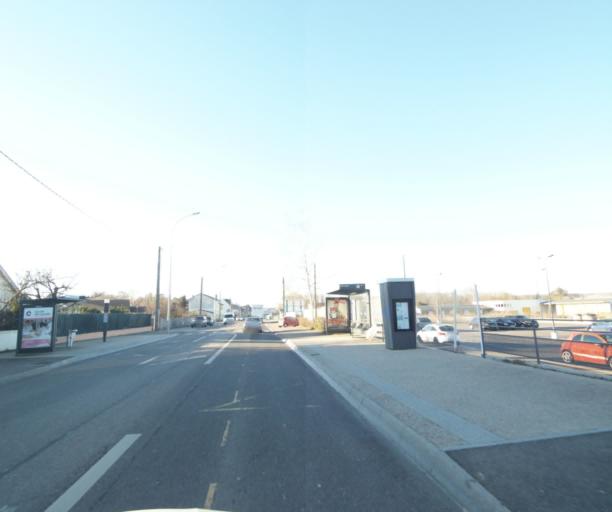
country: FR
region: Lorraine
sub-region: Departement de Meurthe-et-Moselle
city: Laneuveville-devant-Nancy
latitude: 48.6613
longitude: 6.2225
